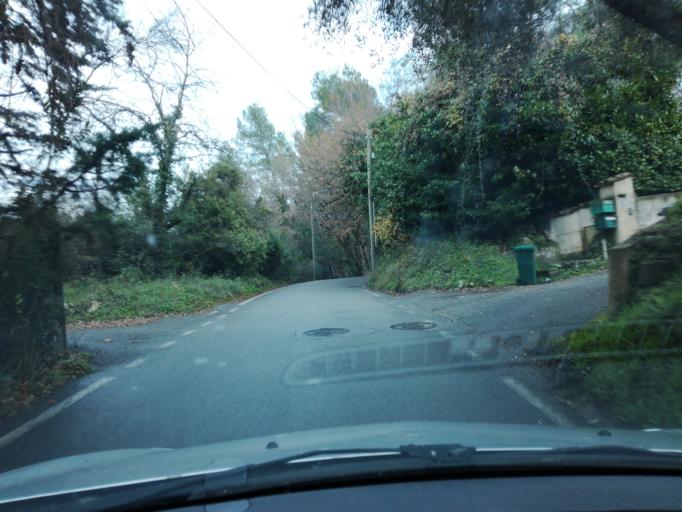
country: FR
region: Provence-Alpes-Cote d'Azur
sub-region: Departement des Alpes-Maritimes
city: Mouans-Sartoux
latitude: 43.6054
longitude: 6.9808
